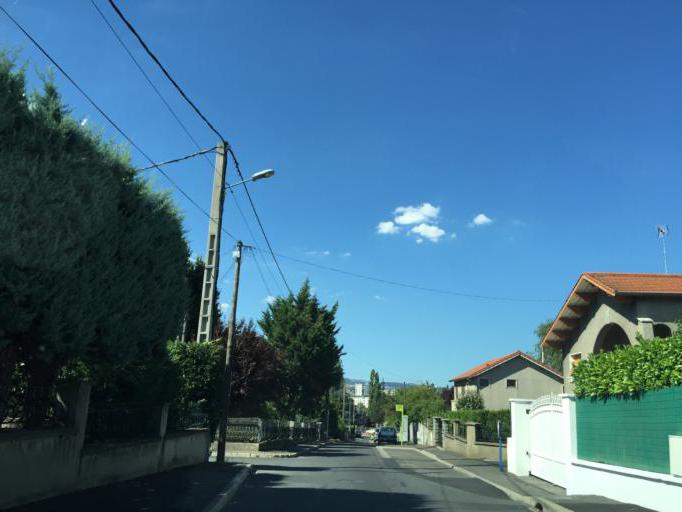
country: FR
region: Rhone-Alpes
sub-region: Departement de la Loire
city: Saint-Chamond
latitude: 45.4682
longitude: 4.5282
